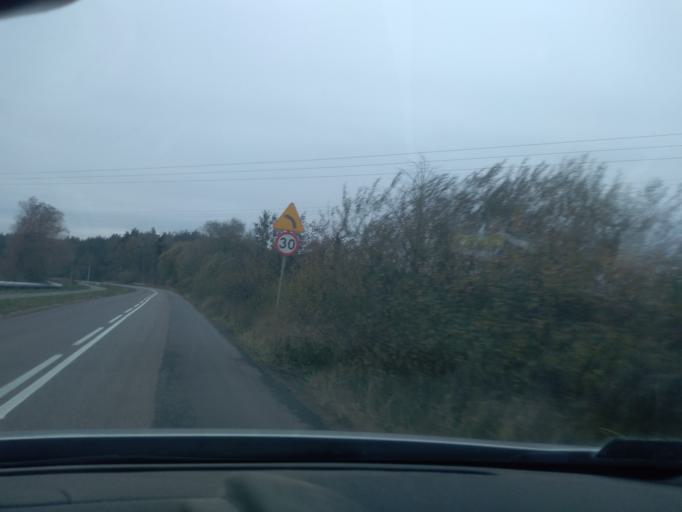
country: PL
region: Greater Poland Voivodeship
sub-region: Powiat poznanski
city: Murowana Goslina
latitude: 52.5579
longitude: 16.9769
